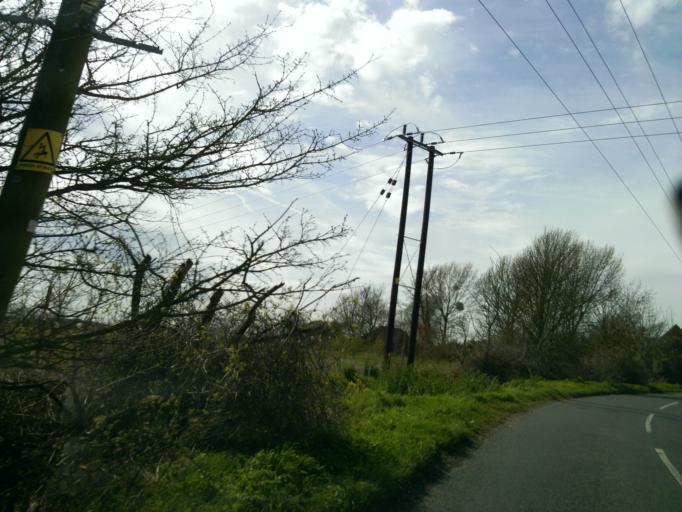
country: GB
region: England
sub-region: Essex
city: Coggeshall
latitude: 51.8414
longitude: 0.6633
